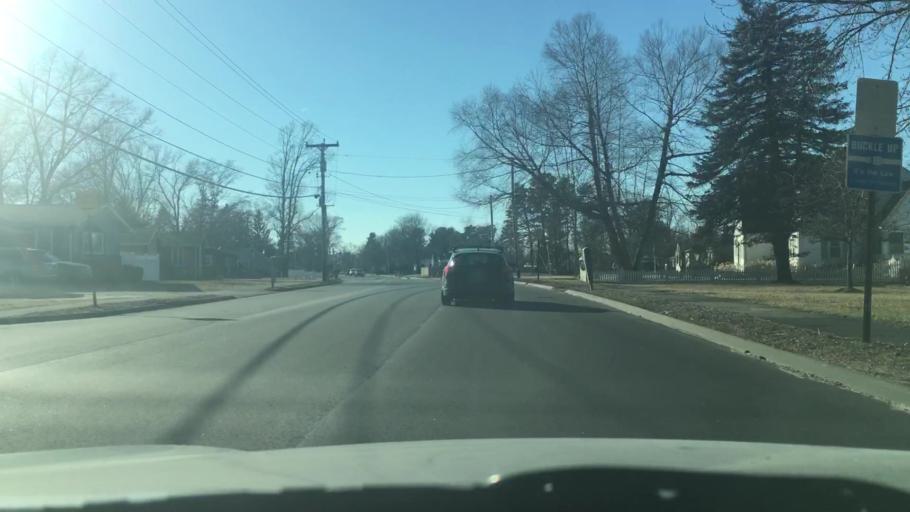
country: US
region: Massachusetts
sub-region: Hampden County
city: Ludlow
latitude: 42.1794
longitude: -72.5195
